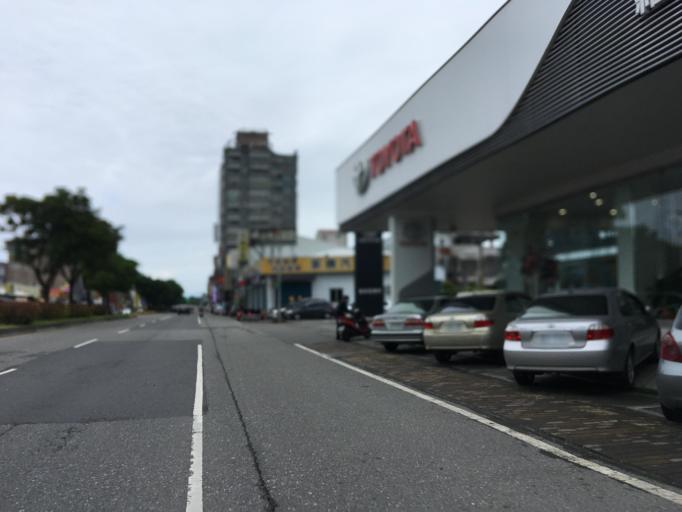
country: TW
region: Taiwan
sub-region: Yilan
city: Yilan
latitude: 24.7061
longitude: 121.7714
